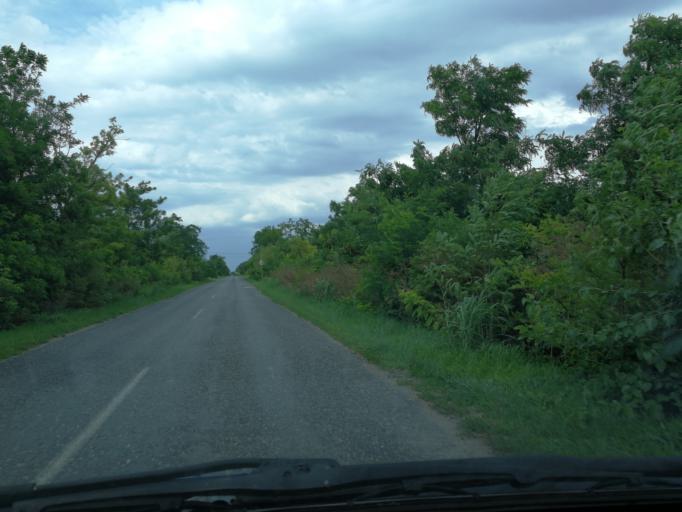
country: HU
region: Bacs-Kiskun
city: Kalocsa
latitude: 46.4720
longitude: 19.0446
